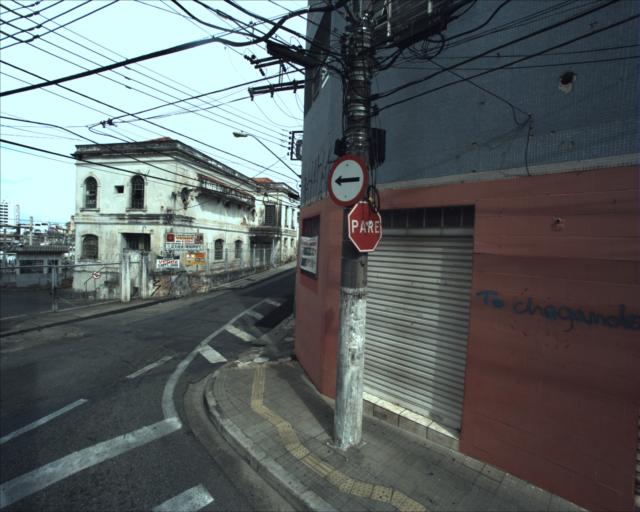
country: BR
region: Sao Paulo
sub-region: Sorocaba
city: Sorocaba
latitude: -23.5008
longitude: -47.4567
